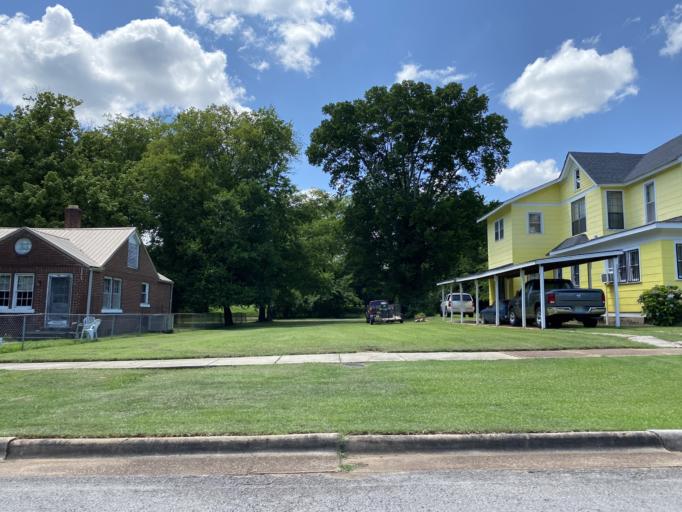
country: US
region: Alabama
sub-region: Morgan County
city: Decatur
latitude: 34.6078
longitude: -86.9926
